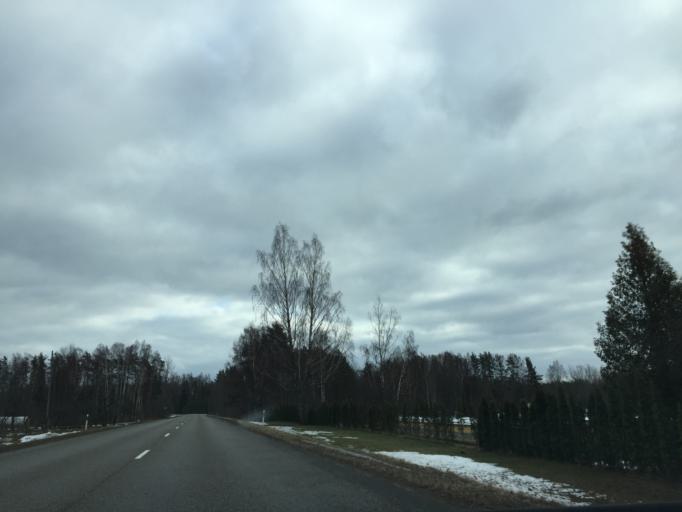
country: LV
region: Salacgrivas
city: Ainazi
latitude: 57.8576
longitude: 24.5119
